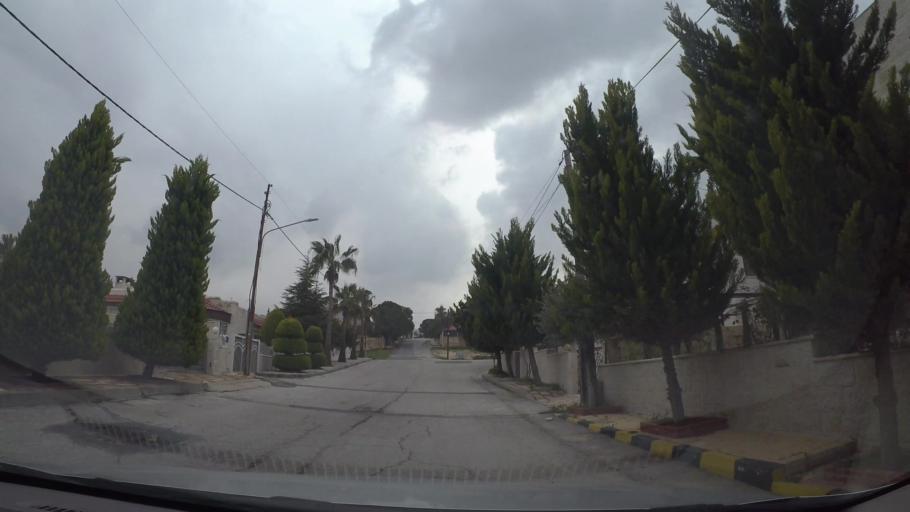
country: JO
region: Amman
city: Umm as Summaq
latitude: 31.8904
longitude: 35.8548
